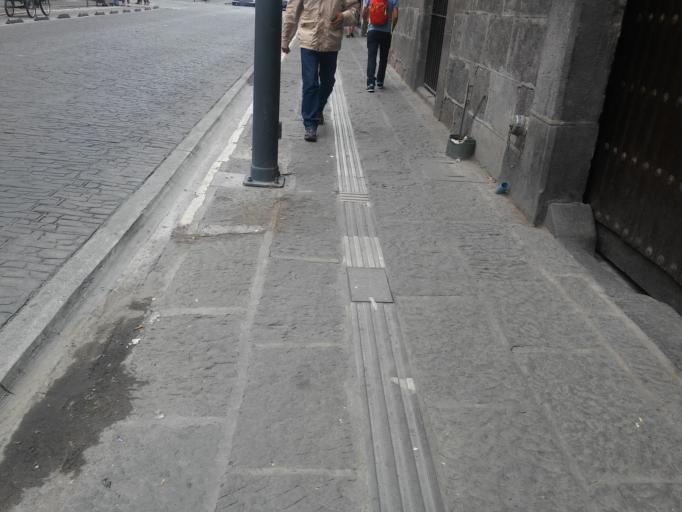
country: MX
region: Puebla
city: Puebla
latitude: 19.0479
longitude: -98.1945
